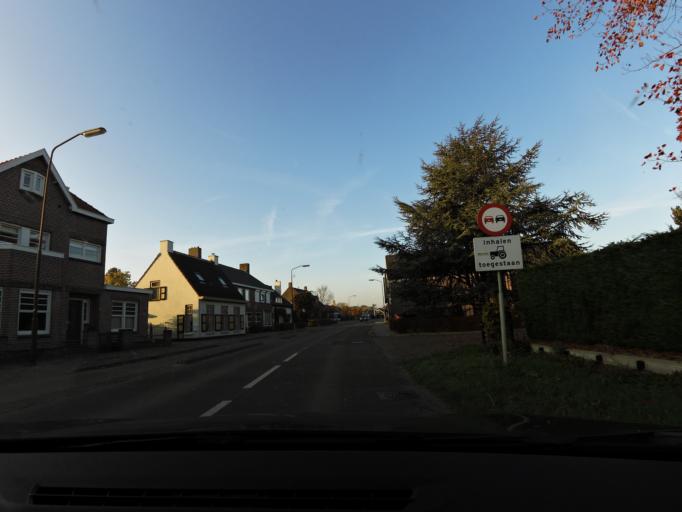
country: NL
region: North Brabant
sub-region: Gemeente Rucphen
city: Rucphen
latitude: 51.5781
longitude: 4.5900
